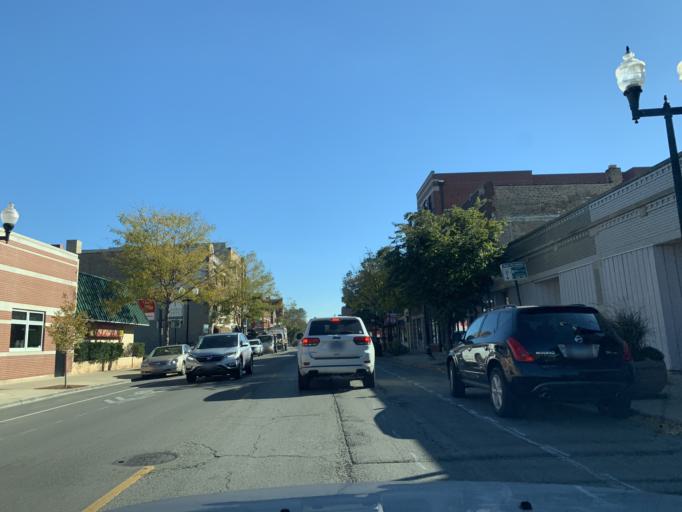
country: US
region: Illinois
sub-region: Cook County
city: Lincolnwood
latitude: 41.9604
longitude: -87.6831
